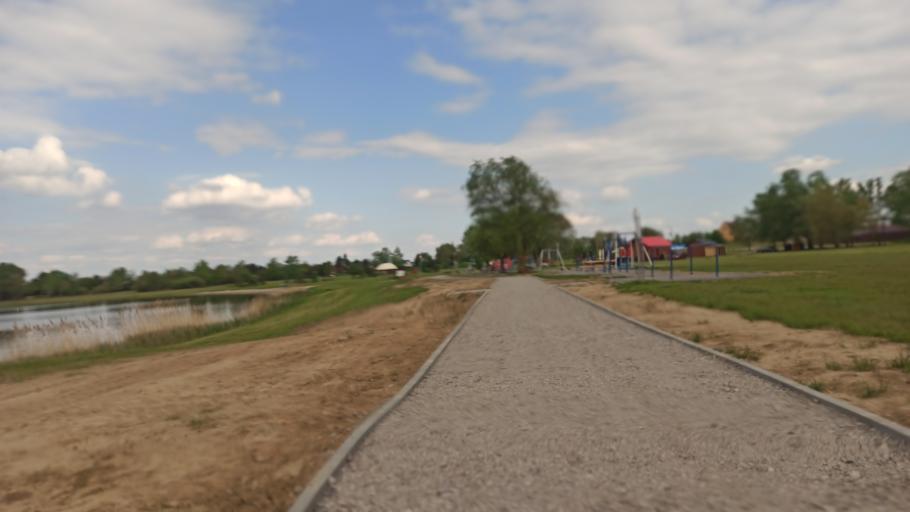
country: PL
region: Subcarpathian Voivodeship
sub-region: Powiat jaroslawski
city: Radymno
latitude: 49.9508
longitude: 22.8266
